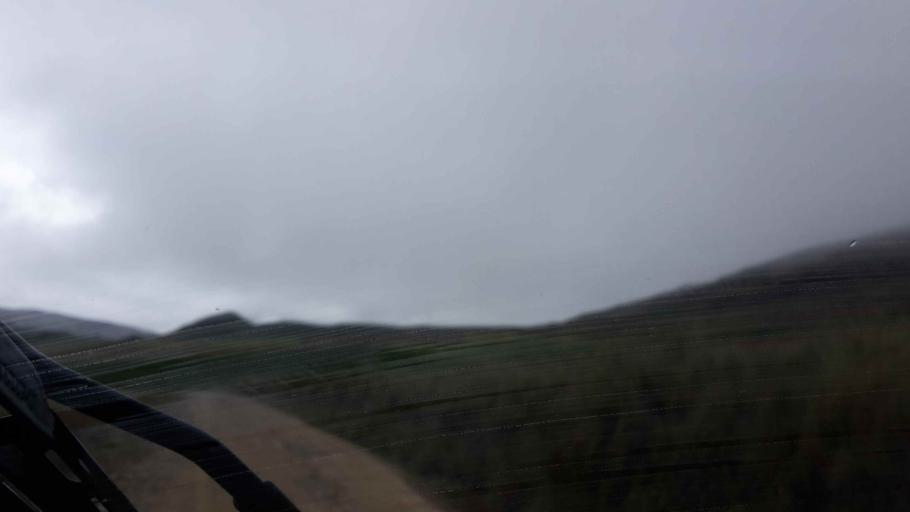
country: BO
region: Cochabamba
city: Cochabamba
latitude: -17.1495
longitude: -66.1029
